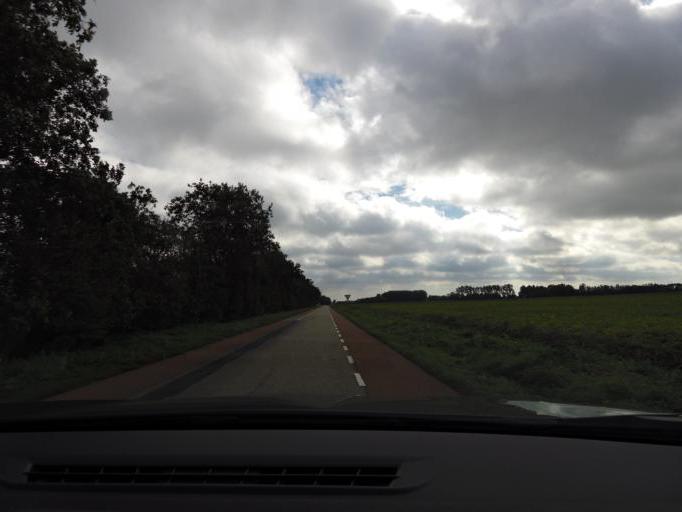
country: NL
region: South Holland
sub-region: Gemeente Goeree-Overflakkee
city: Dirksland
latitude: 51.7836
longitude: 4.0469
